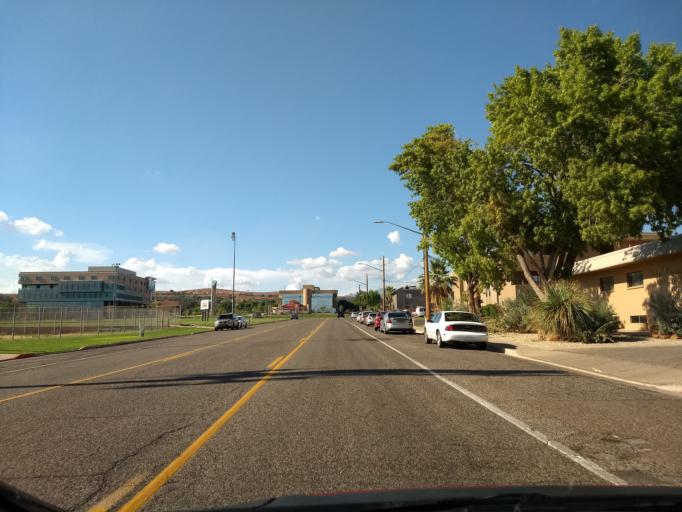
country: US
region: Utah
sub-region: Washington County
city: Saint George
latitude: 37.0997
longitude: -113.5643
